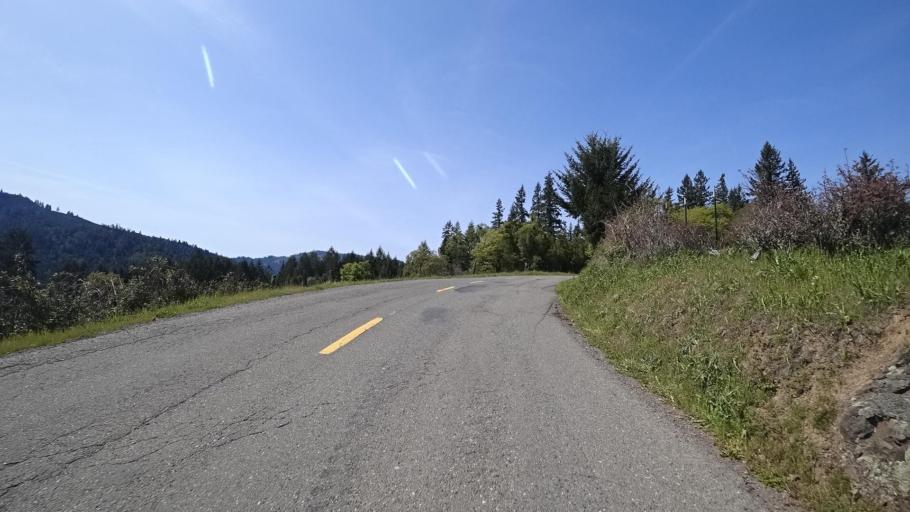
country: US
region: California
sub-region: Humboldt County
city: Redway
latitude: 40.3919
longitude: -123.7469
